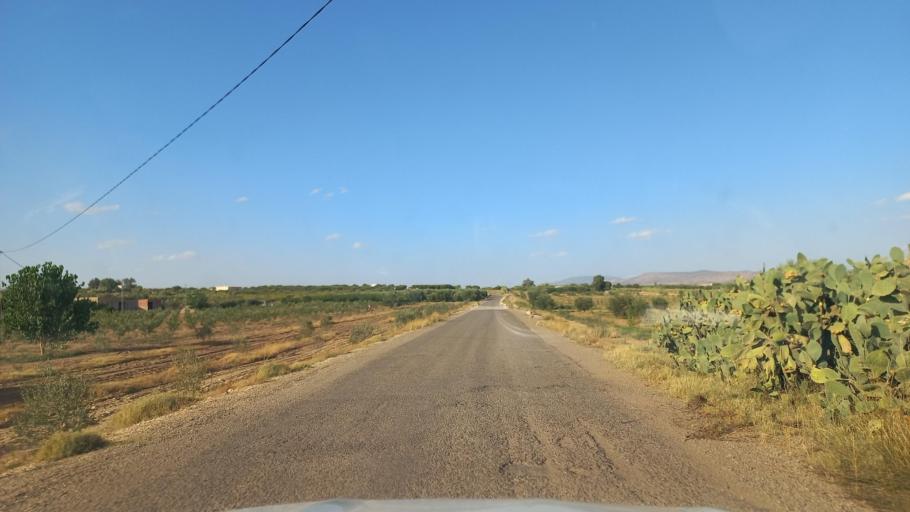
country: TN
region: Al Qasrayn
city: Kasserine
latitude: 35.2670
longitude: 9.0276
